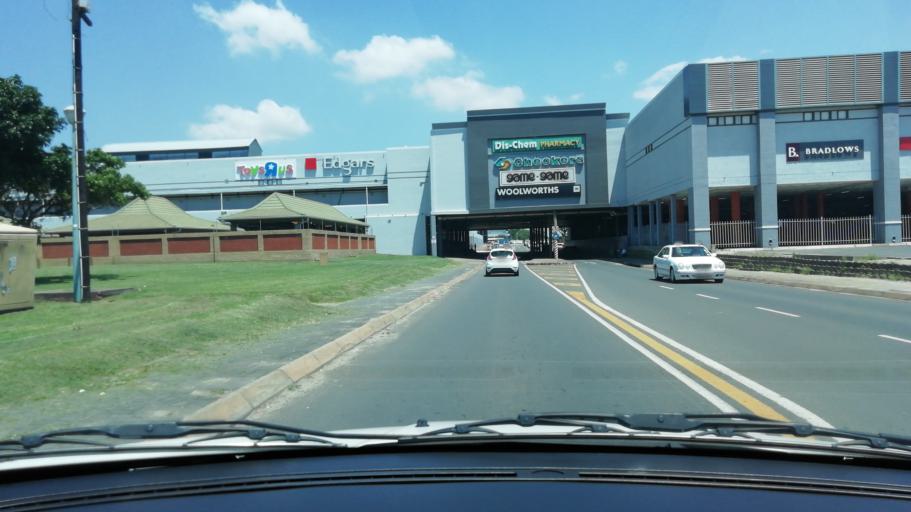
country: ZA
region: KwaZulu-Natal
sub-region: uThungulu District Municipality
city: Richards Bay
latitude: -28.7549
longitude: 32.0507
